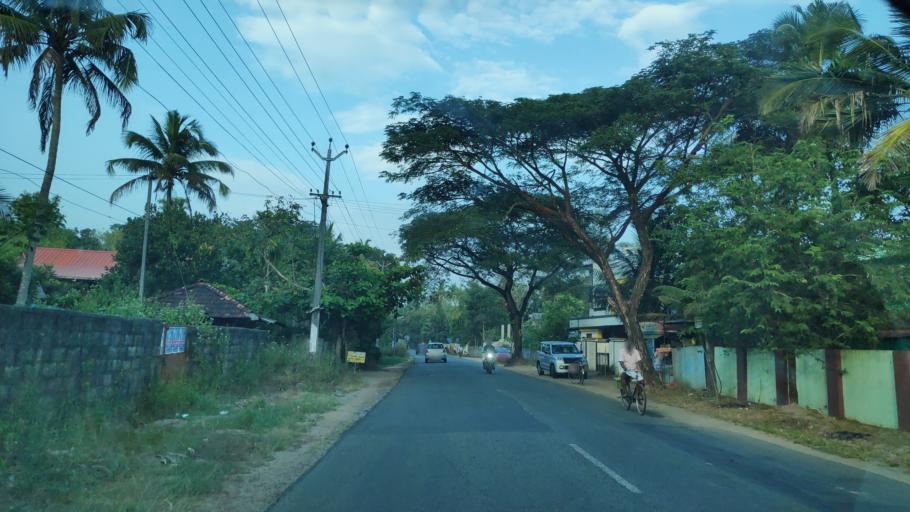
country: IN
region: Kerala
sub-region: Alappuzha
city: Shertallai
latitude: 9.6244
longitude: 76.3666
